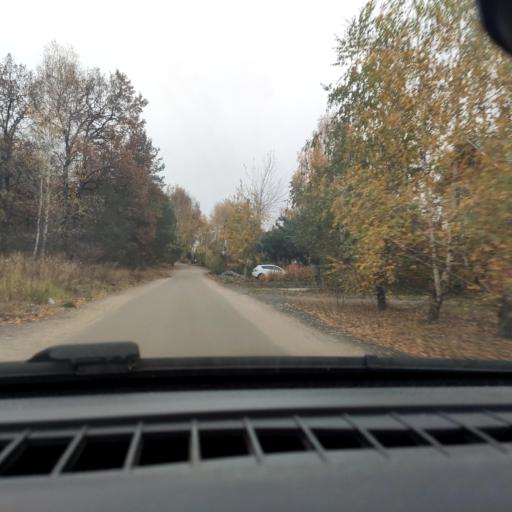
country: RU
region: Voronezj
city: Podgornoye
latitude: 51.7646
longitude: 39.1819
